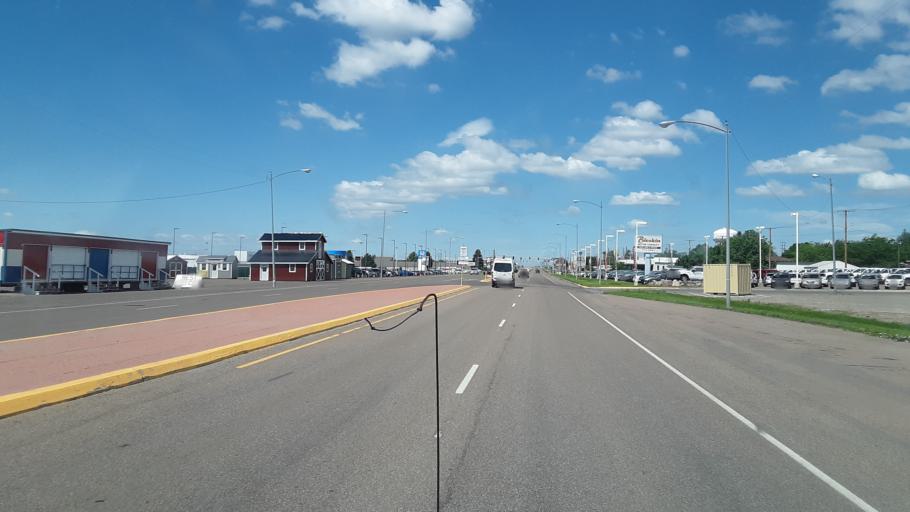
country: US
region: Montana
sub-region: Cascade County
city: Malmstrom Air Force Base
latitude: 47.4939
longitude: -111.2221
